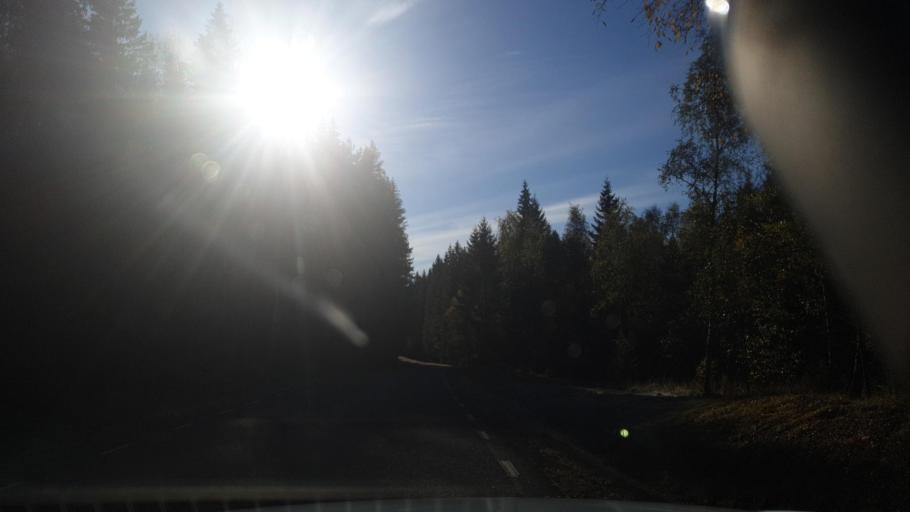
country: SE
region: Vaermland
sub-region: Karlstads Kommun
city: Edsvalla
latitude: 59.5311
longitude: 13.1110
